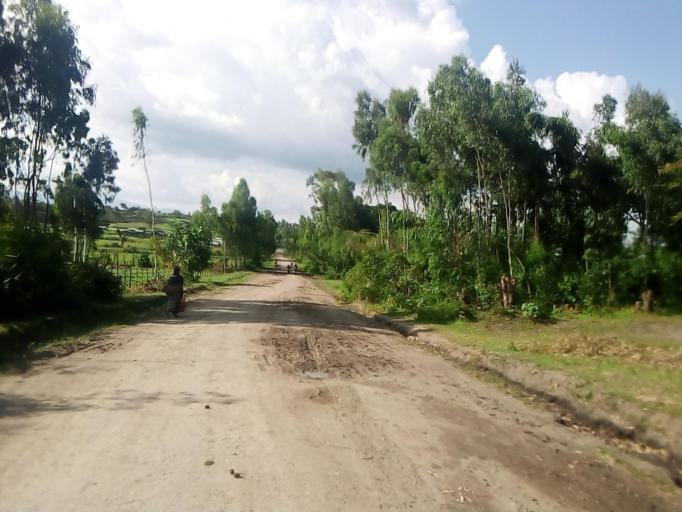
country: ET
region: Southern Nations, Nationalities, and People's Region
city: K'olito
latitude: 7.6610
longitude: 38.0477
